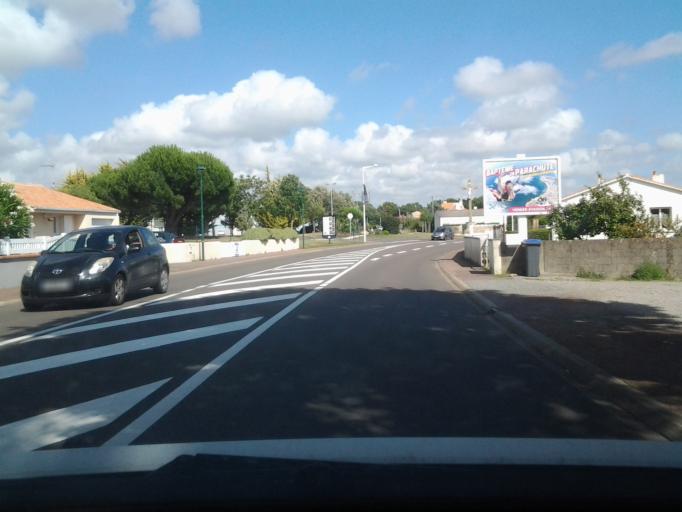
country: FR
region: Pays de la Loire
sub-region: Departement de la Vendee
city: Olonne-sur-Mer
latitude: 46.5344
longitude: -1.7631
